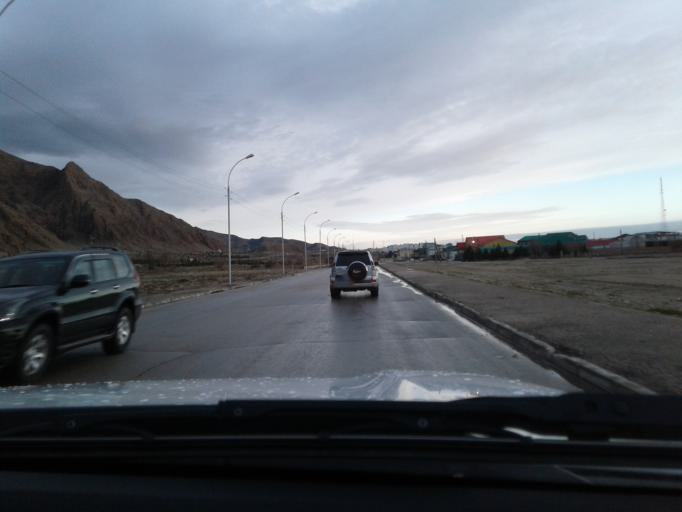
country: TM
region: Balkan
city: Balkanabat
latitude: 39.5309
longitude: 54.3553
